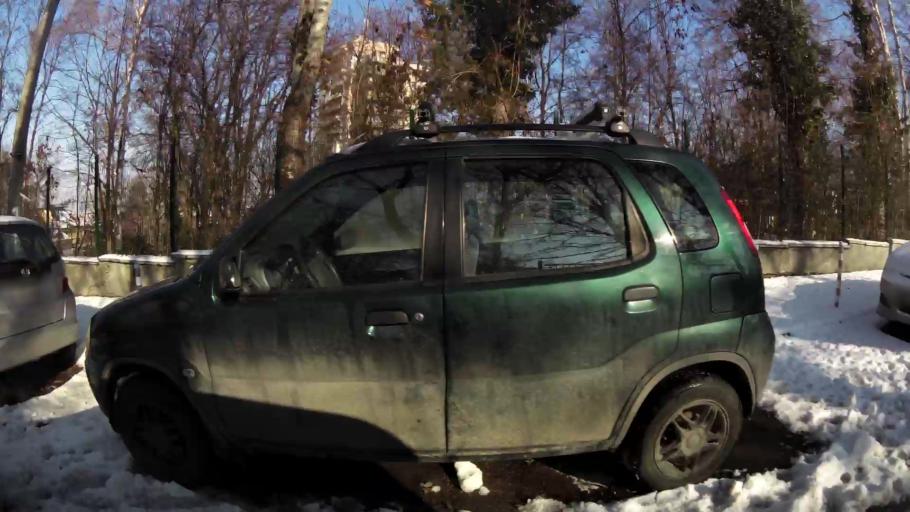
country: BG
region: Sofia-Capital
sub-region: Stolichna Obshtina
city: Sofia
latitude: 42.6772
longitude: 23.3297
